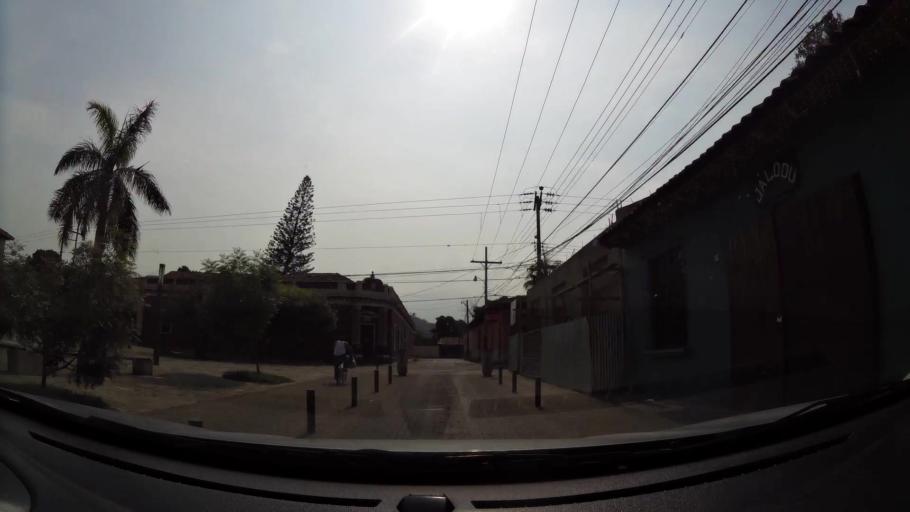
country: HN
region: Comayagua
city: Comayagua
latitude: 14.4616
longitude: -87.6407
